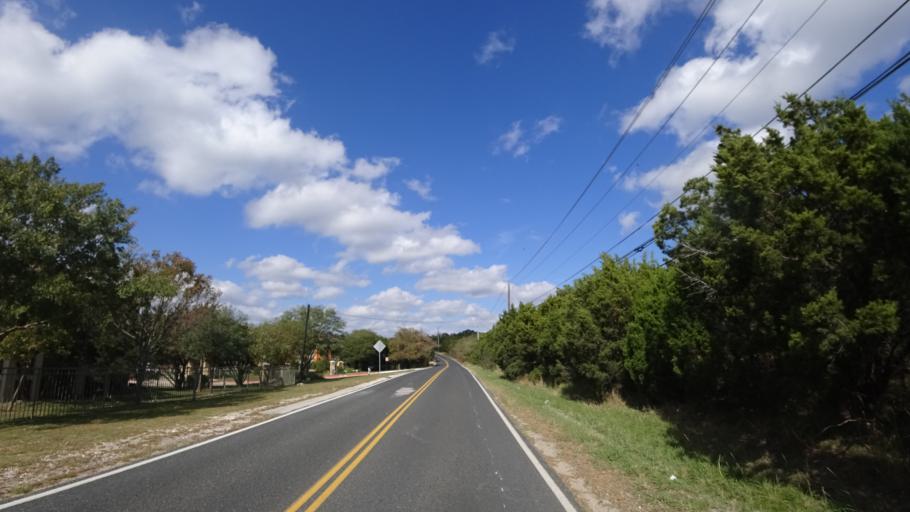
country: US
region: Texas
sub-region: Travis County
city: Barton Creek
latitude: 30.2508
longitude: -97.8869
